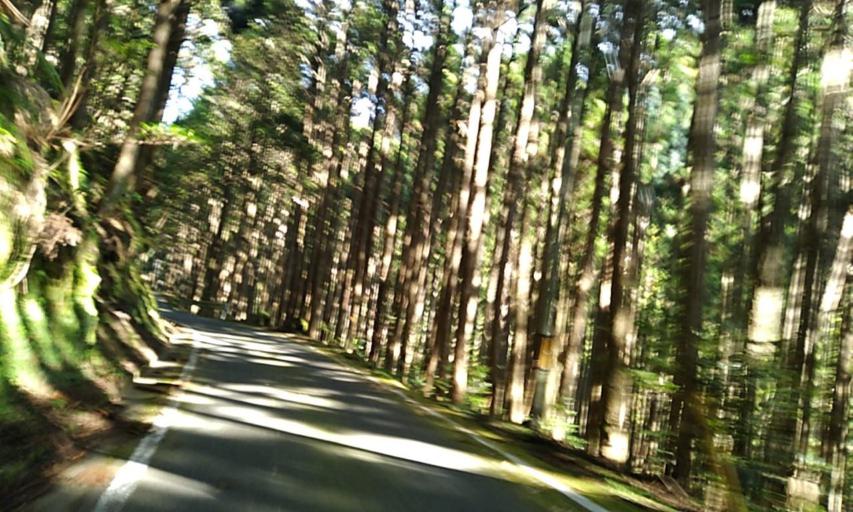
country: JP
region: Wakayama
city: Shingu
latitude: 33.9139
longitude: 135.9903
